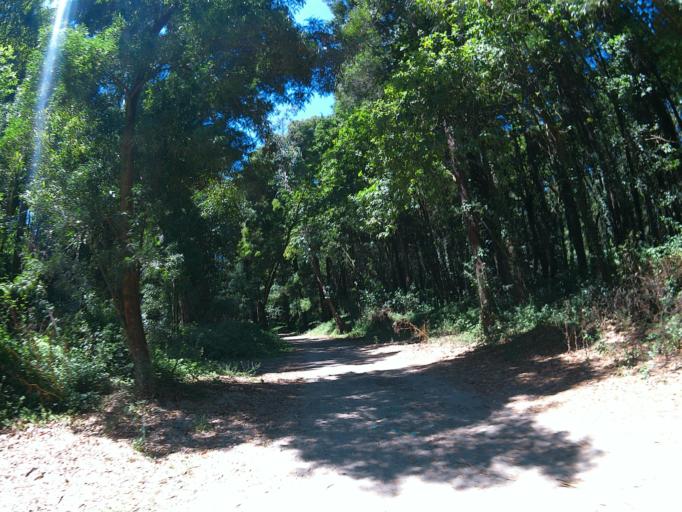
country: PT
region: Viana do Castelo
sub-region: Viana do Castelo
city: Darque
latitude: 41.7087
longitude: -8.7230
